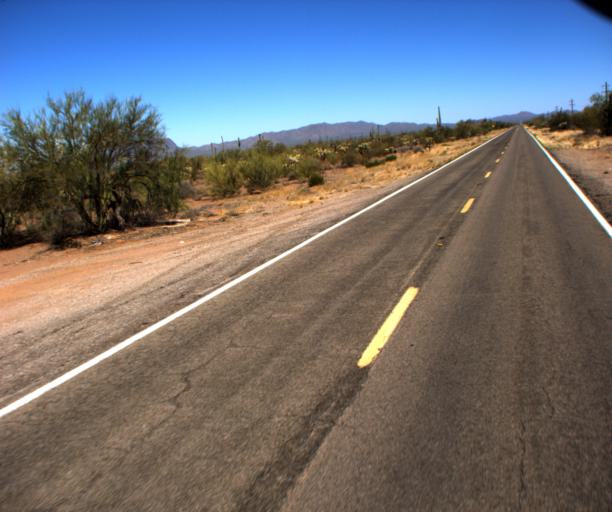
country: US
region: Arizona
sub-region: Pima County
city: Sells
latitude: 32.0194
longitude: -112.0007
